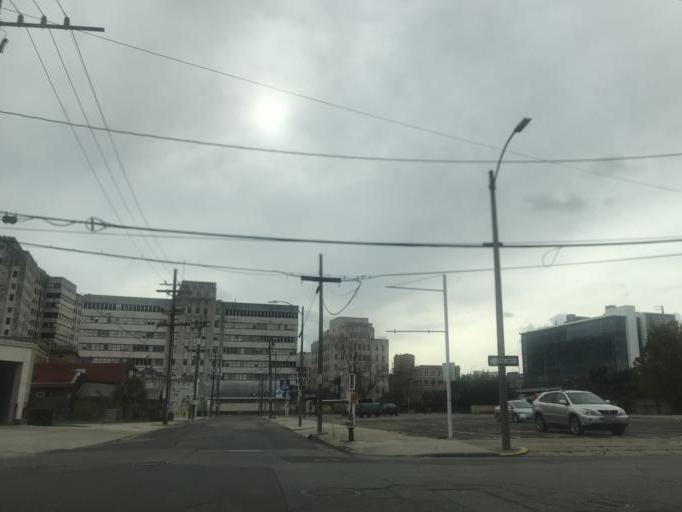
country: US
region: Louisiana
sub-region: Orleans Parish
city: New Orleans
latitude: 29.9576
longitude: -90.0777
